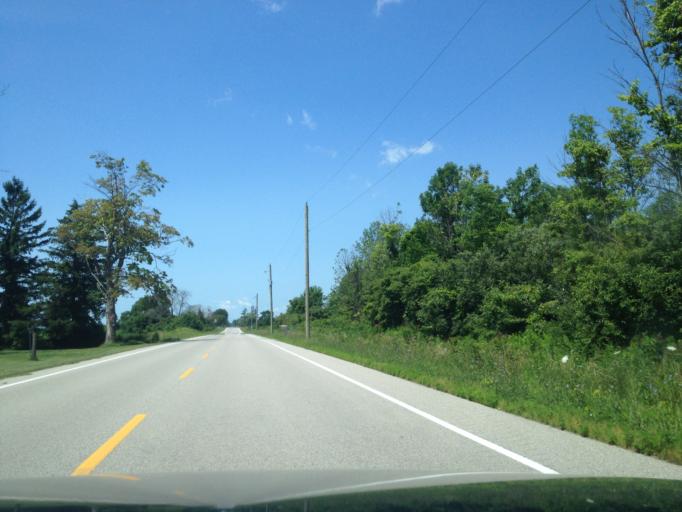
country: CA
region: Ontario
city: Norfolk County
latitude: 42.5781
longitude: -80.5594
